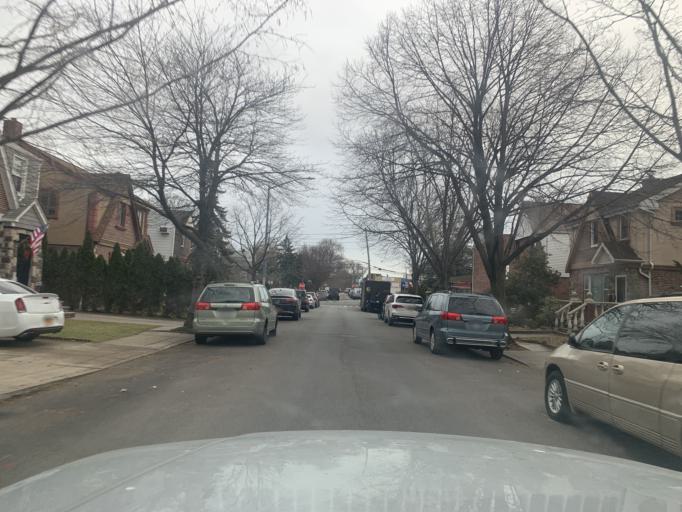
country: US
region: New York
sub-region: Queens County
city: Borough of Queens
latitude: 40.7238
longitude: -73.8749
